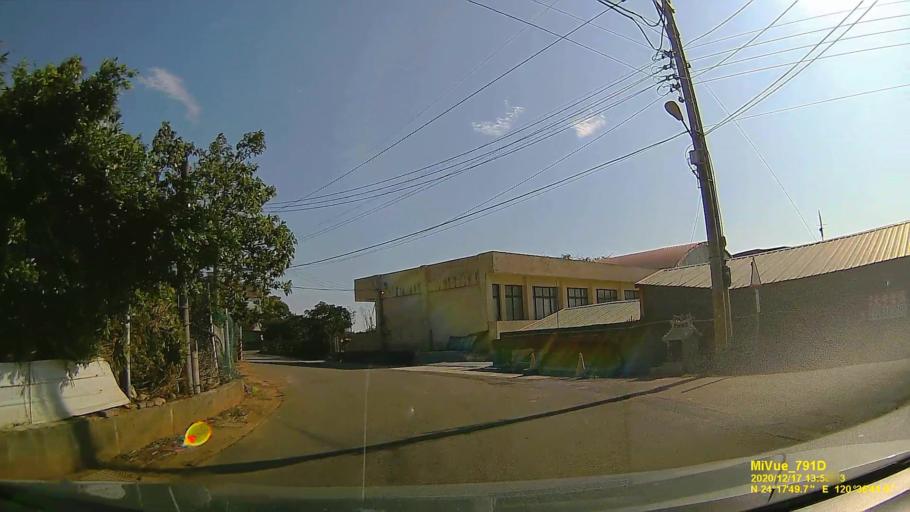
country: TW
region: Taiwan
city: Fengyuan
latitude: 24.2971
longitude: 120.6114
